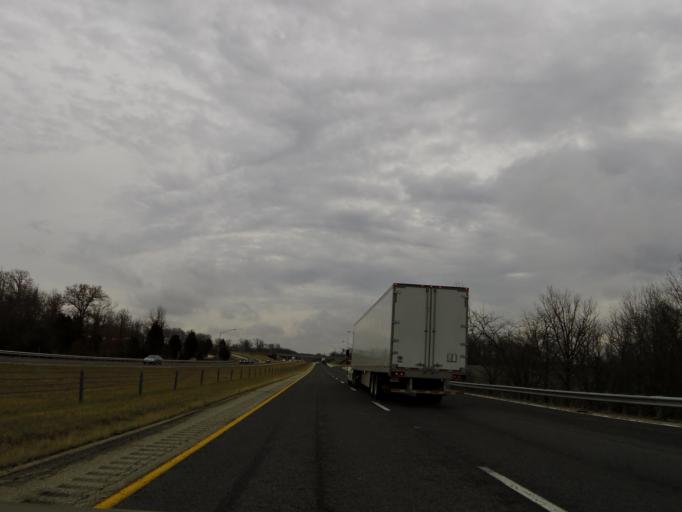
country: US
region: Indiana
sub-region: Ripley County
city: Sunman
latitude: 39.2803
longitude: -85.1065
